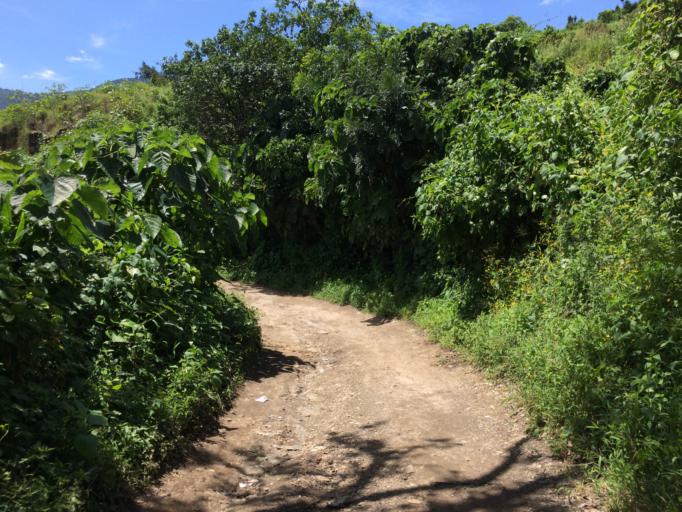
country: GT
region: Guatemala
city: Amatitlan
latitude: 14.4899
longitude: -90.6449
